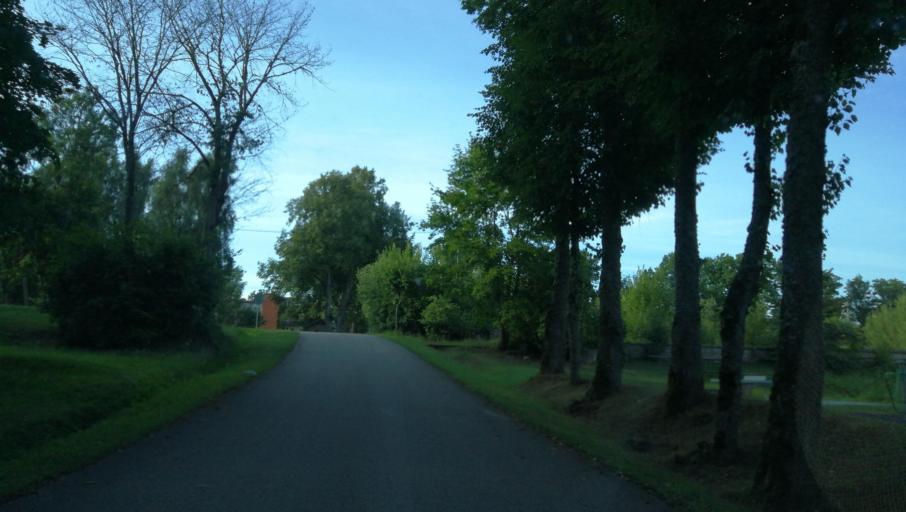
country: LV
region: Pargaujas
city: Stalbe
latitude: 57.3346
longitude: 25.1408
